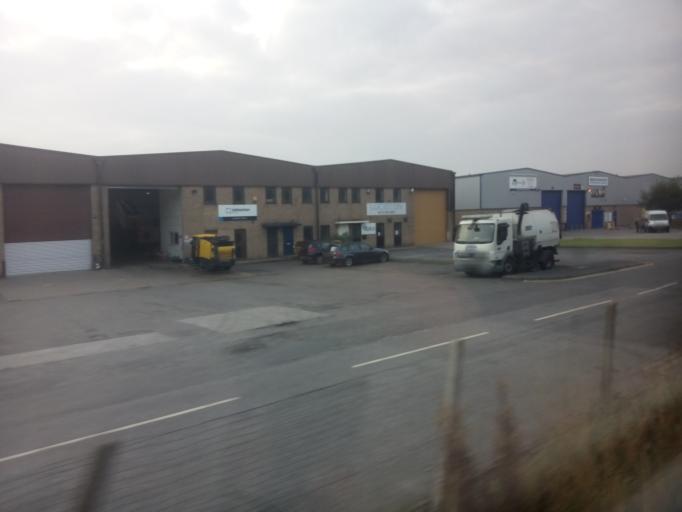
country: GB
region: England
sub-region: City and Borough of Leeds
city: Leeds
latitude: 53.7895
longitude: -1.5714
